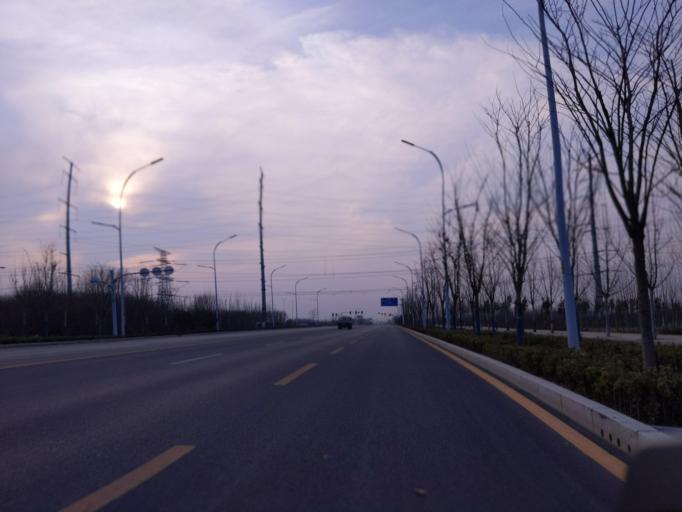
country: CN
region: Henan Sheng
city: Puyang
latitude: 35.8189
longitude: 114.9991
